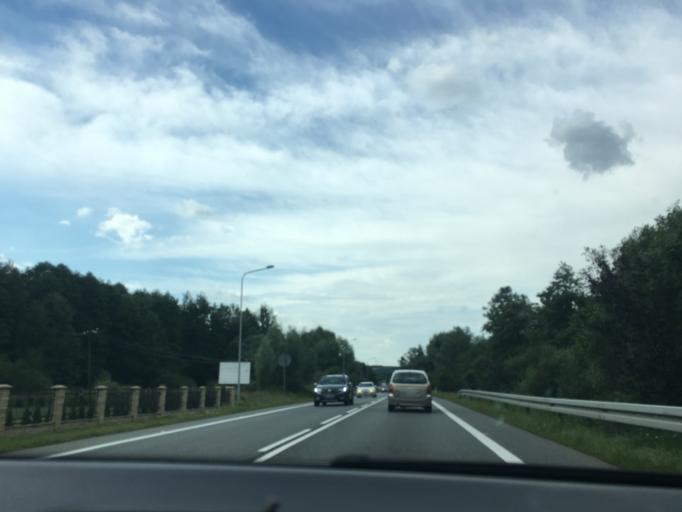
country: PL
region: Subcarpathian Voivodeship
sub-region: Powiat strzyzowski
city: Polomia
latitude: 49.8819
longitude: 21.9021
